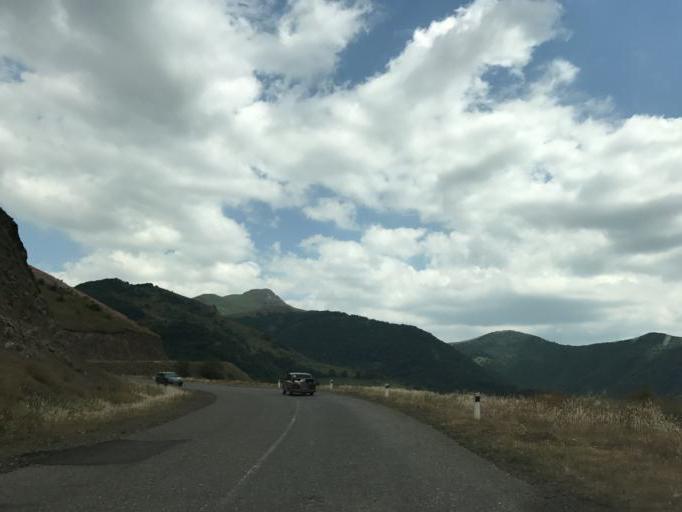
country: AZ
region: Lacin
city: Lacin
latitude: 39.6834
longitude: 46.6359
